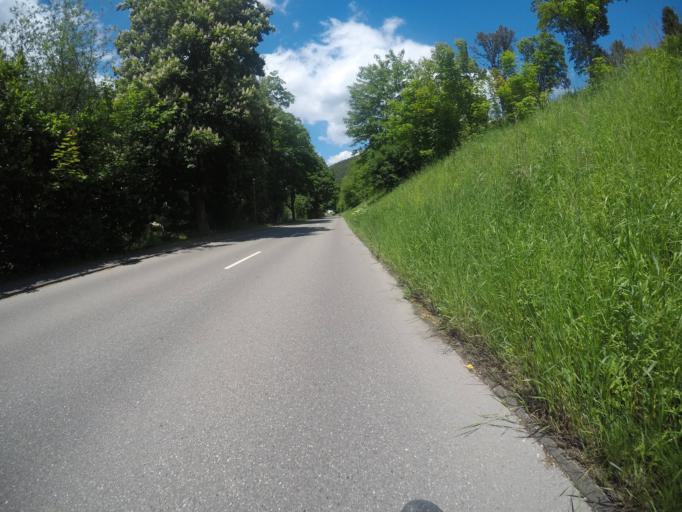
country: DE
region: Baden-Wuerttemberg
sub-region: Karlsruhe Region
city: Bad Liebenzell
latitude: 48.7782
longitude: 8.7334
